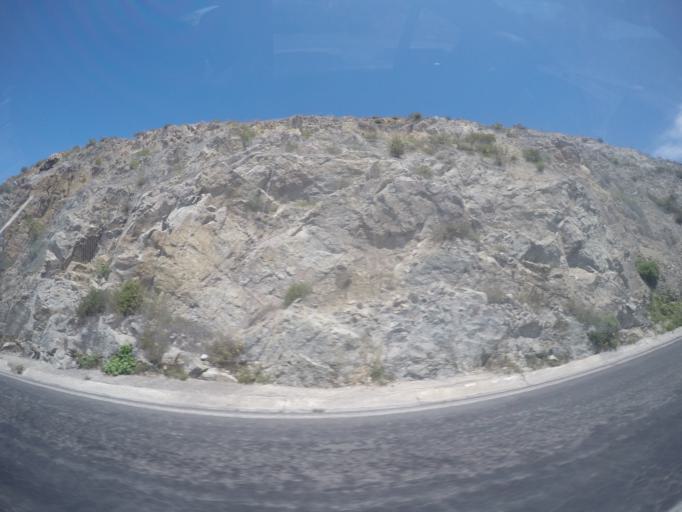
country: MX
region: Hidalgo
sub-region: Mineral de la Reforma
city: Guadalupe Minerva
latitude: 20.1291
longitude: -98.6949
